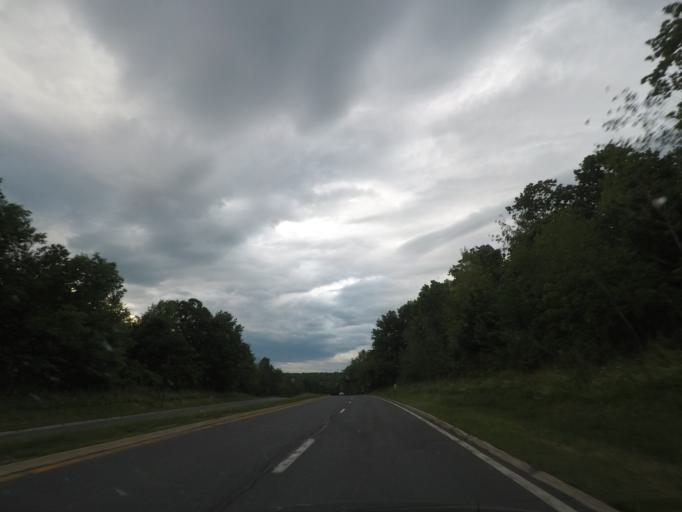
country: US
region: New York
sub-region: Dutchess County
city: Pine Plains
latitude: 42.0849
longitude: -73.7193
